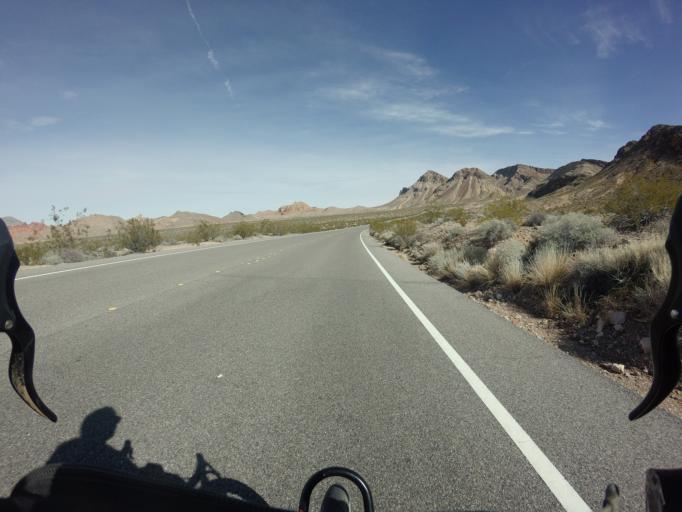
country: US
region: Nevada
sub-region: Clark County
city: Boulder City
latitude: 36.2113
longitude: -114.6557
